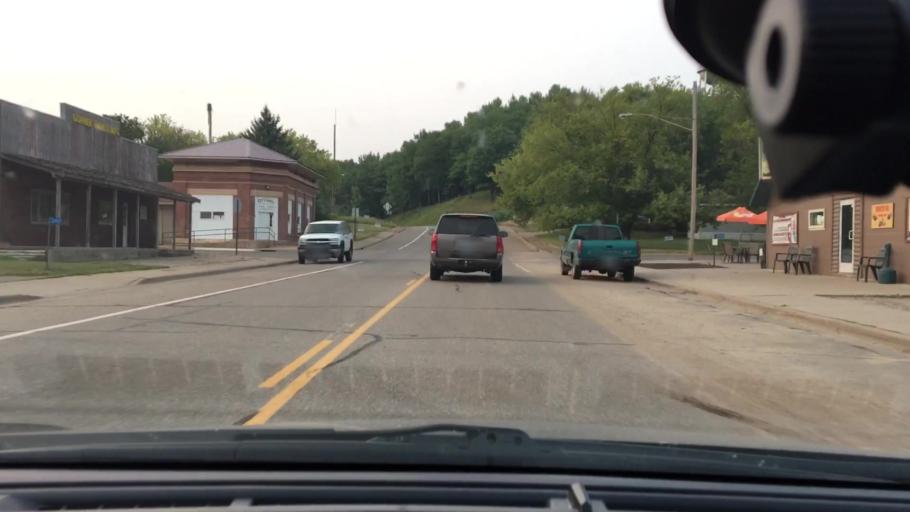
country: US
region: Minnesota
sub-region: Crow Wing County
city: Crosby
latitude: 46.5174
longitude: -93.9233
